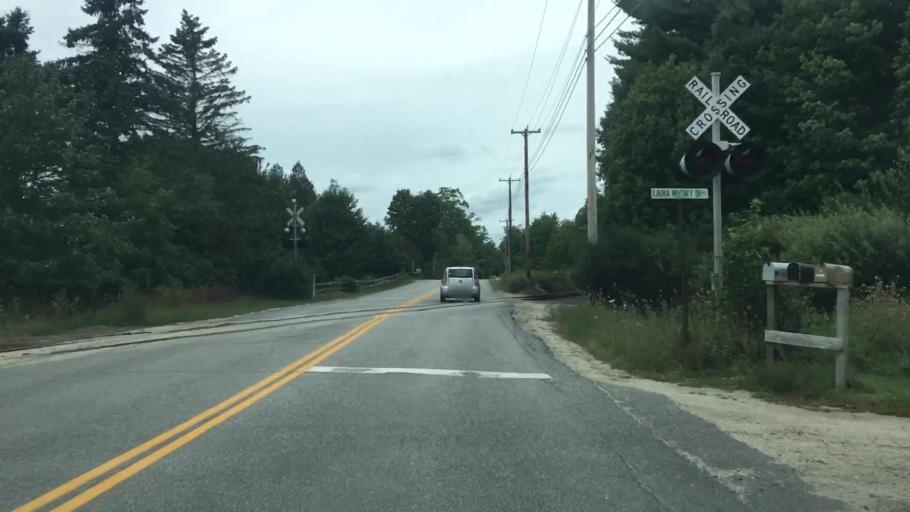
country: US
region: Maine
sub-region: Cumberland County
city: Yarmouth
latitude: 43.8407
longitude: -70.2086
